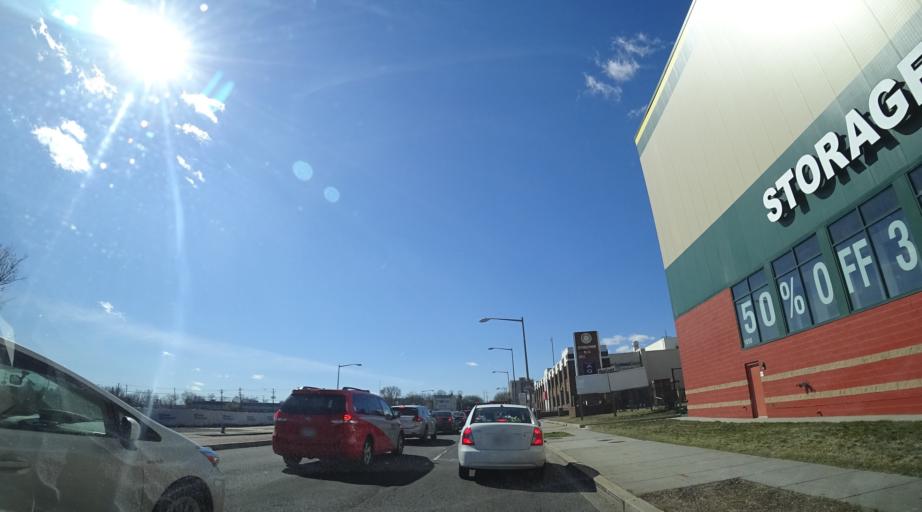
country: US
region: Maryland
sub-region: Prince George's County
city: Mount Rainier
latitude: 38.9175
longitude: -76.9754
